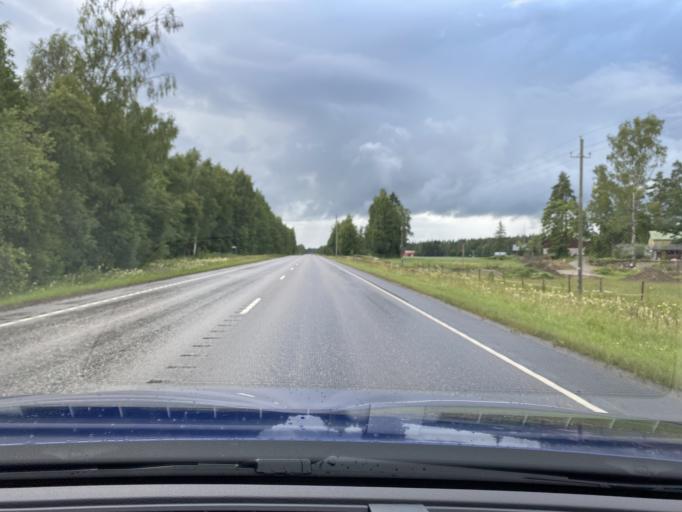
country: FI
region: Uusimaa
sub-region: Helsinki
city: Nurmijaervi
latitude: 60.5454
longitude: 24.8307
